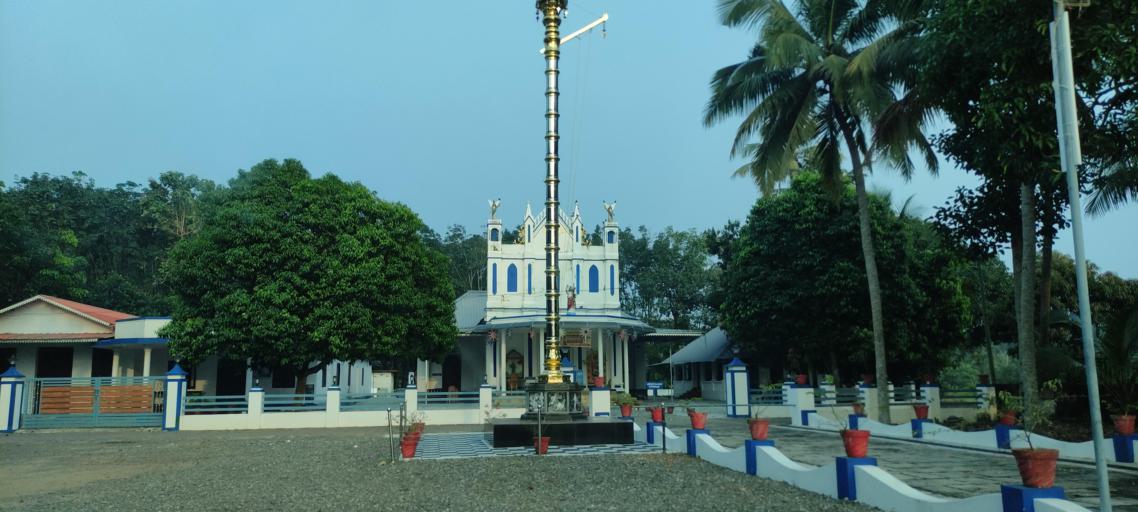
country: IN
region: Kerala
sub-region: Kottayam
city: Vaikam
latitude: 9.6802
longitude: 76.4643
